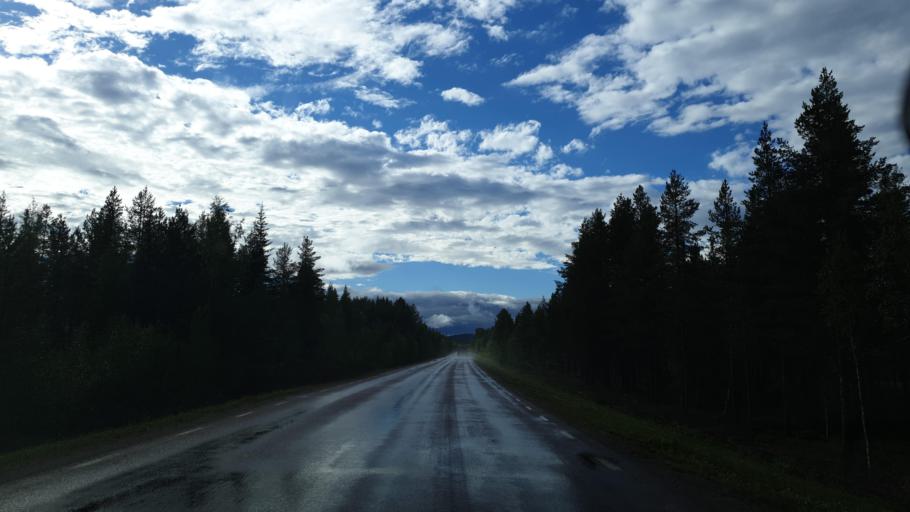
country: SE
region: Norrbotten
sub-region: Arjeplogs Kommun
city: Arjeplog
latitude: 66.0046
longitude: 18.1126
